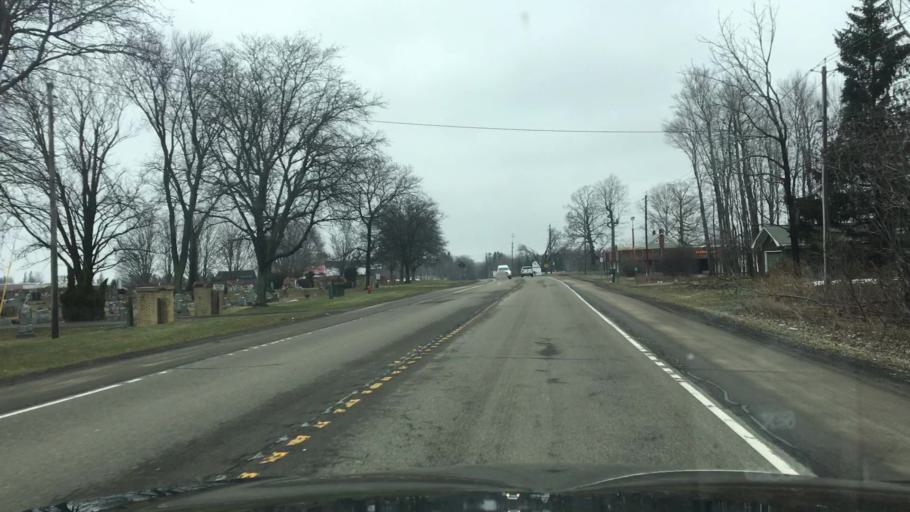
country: US
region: New York
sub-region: Chautauqua County
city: Fredonia
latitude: 42.4406
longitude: -79.3053
